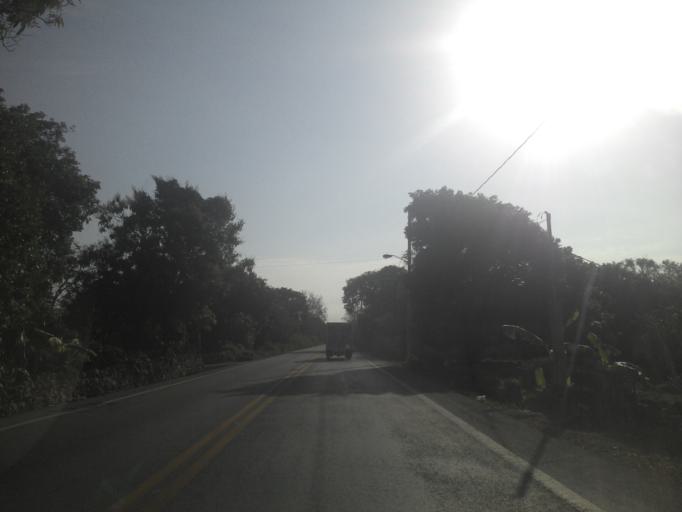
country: MX
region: Yucatan
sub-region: Valladolid
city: Tikuch
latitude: 20.7014
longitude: -88.1126
